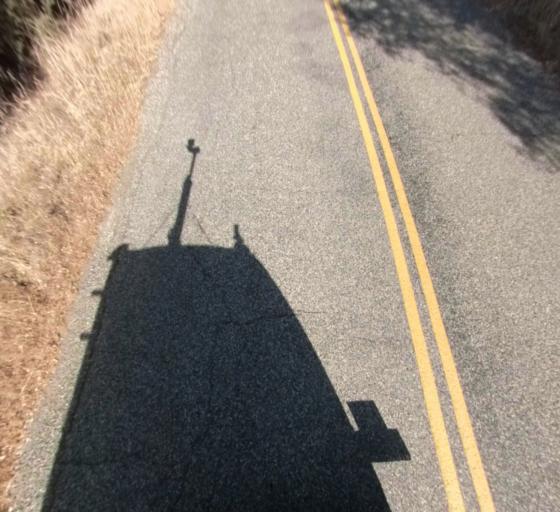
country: US
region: California
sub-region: Fresno County
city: Auberry
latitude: 37.1858
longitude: -119.4567
